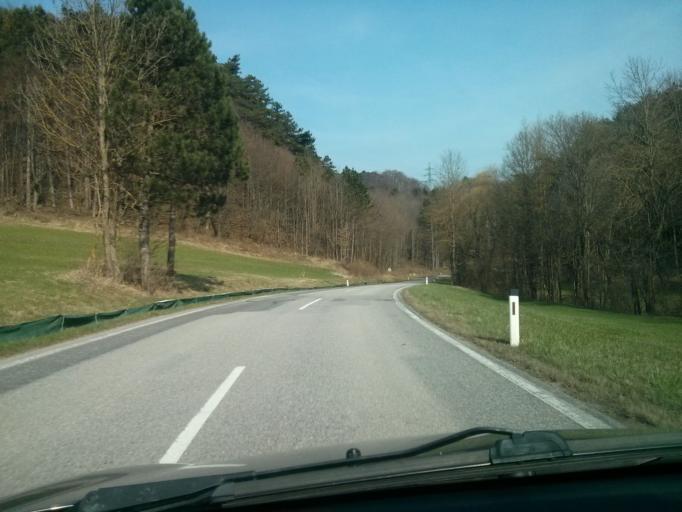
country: AT
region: Lower Austria
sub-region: Politischer Bezirk Baden
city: Hernstein
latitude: 47.8992
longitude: 16.0967
